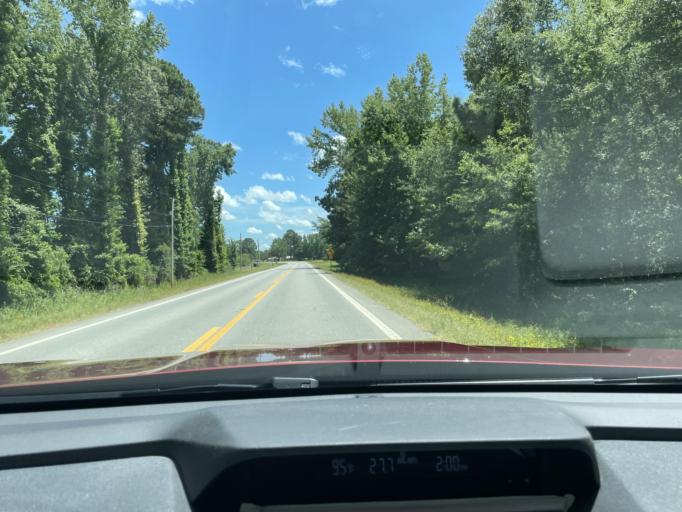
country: US
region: Arkansas
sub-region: Drew County
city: Monticello
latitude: 33.6073
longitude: -91.7365
